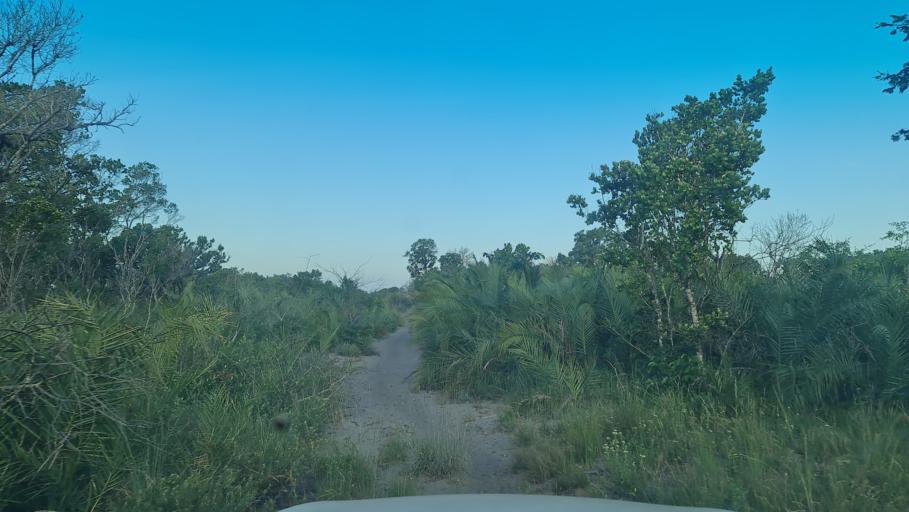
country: MZ
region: Gaza
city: Macia
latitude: -25.2178
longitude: 33.0455
